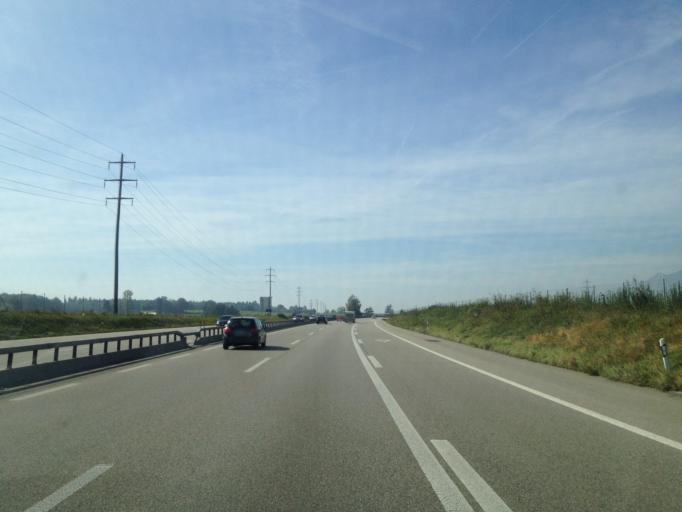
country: CH
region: Bern
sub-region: Oberaargau
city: Niederbipp
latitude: 47.2591
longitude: 7.7026
